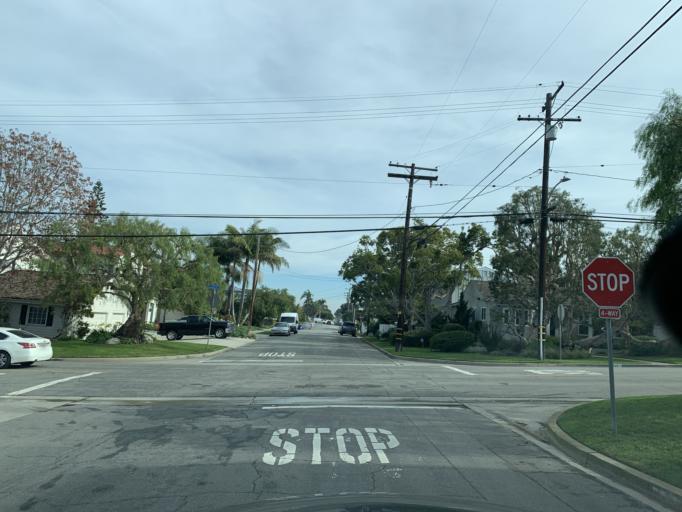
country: US
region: California
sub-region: Los Angeles County
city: Manhattan Beach
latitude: 33.8838
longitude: -118.3984
